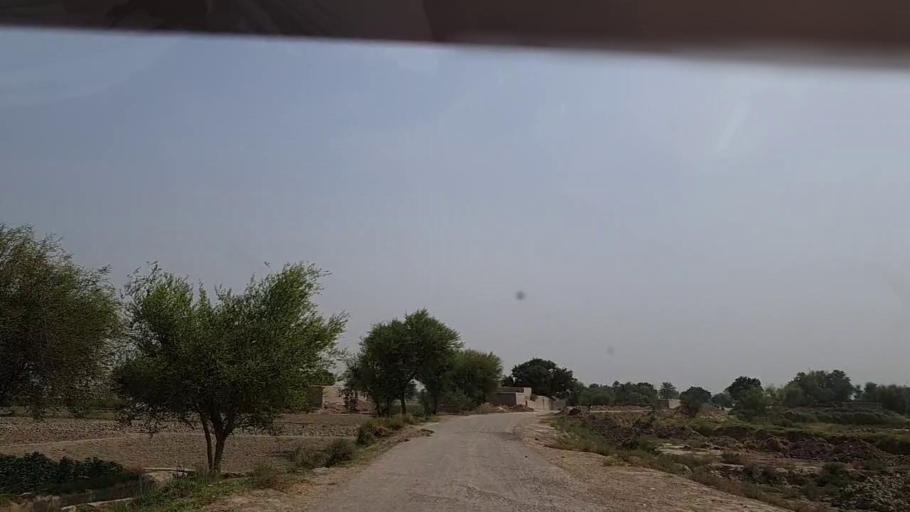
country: PK
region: Sindh
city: Khairpur Nathan Shah
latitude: 27.0551
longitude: 67.6843
